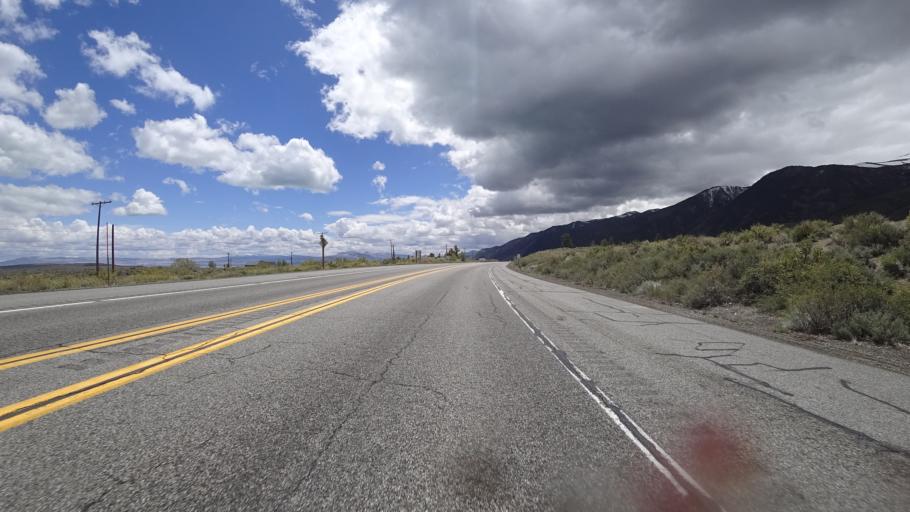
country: US
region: California
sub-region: Mono County
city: Bridgeport
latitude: 38.0433
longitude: -119.1597
